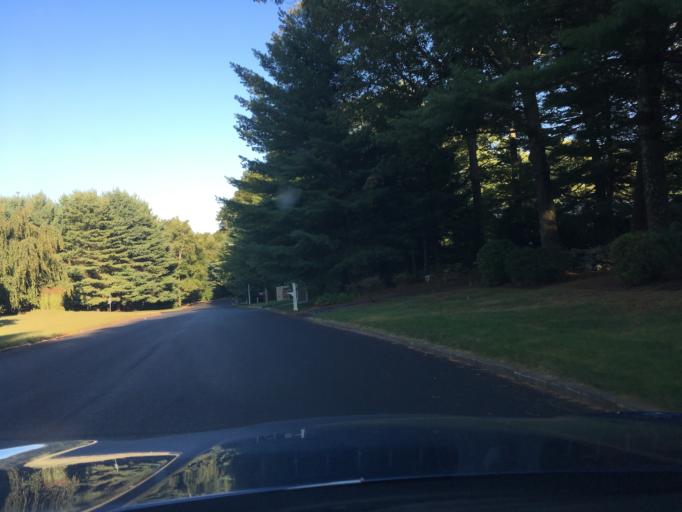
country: US
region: Rhode Island
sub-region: Kent County
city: West Warwick
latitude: 41.6463
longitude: -71.5171
